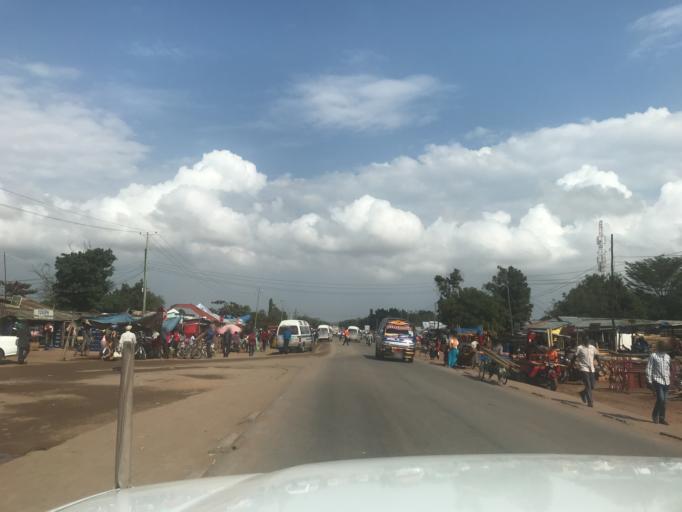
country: TZ
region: Mwanza
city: Usagara
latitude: -2.5554
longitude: 33.0480
